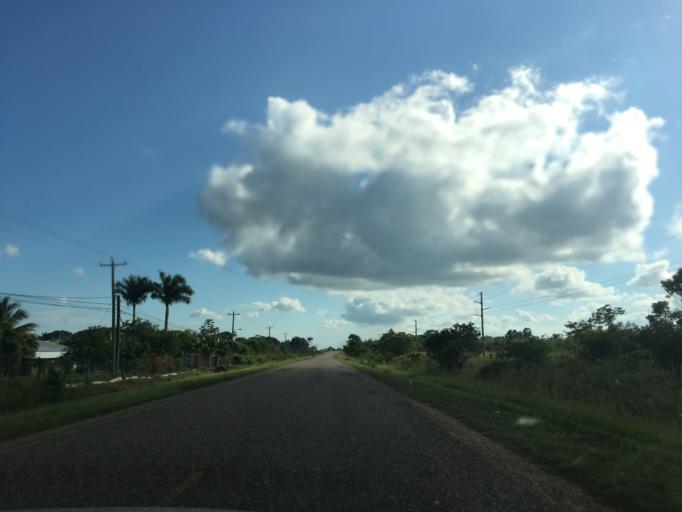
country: BZ
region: Stann Creek
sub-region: Dangriga
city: Dangriga
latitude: 16.8693
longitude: -88.3481
